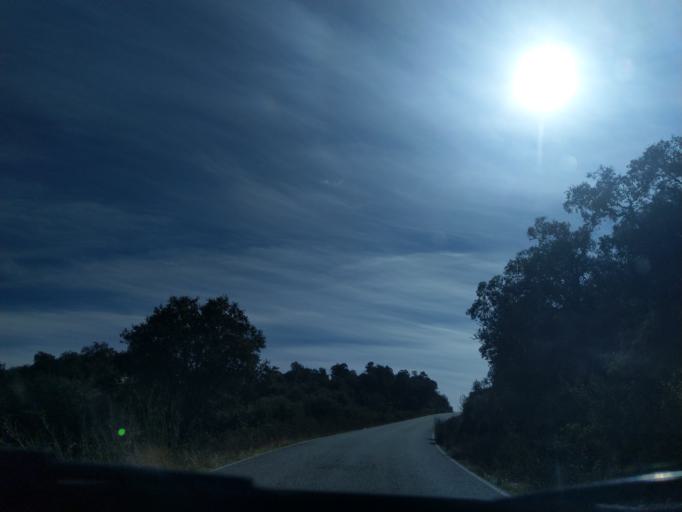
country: ES
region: Extremadura
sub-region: Provincia de Badajoz
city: Reina
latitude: 38.1313
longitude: -5.9158
